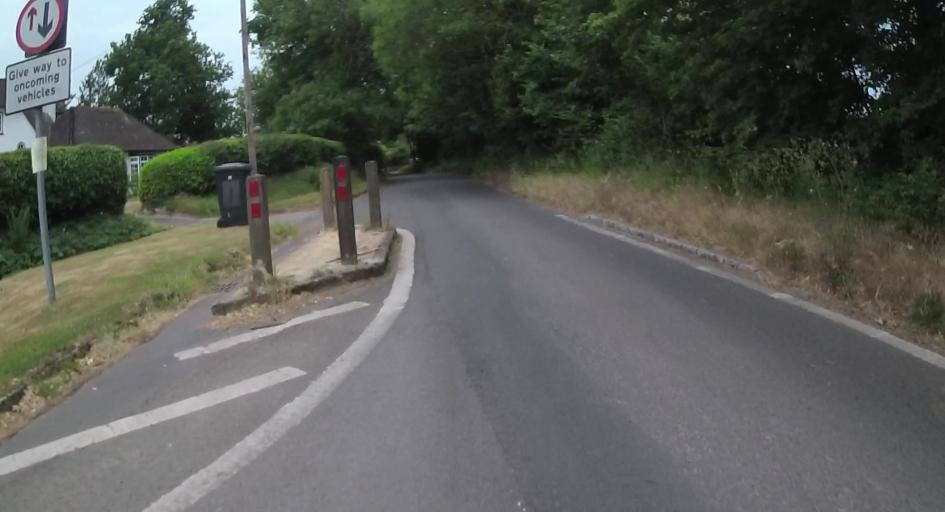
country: GB
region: England
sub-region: Hampshire
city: Fleet
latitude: 51.2686
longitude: -0.8772
